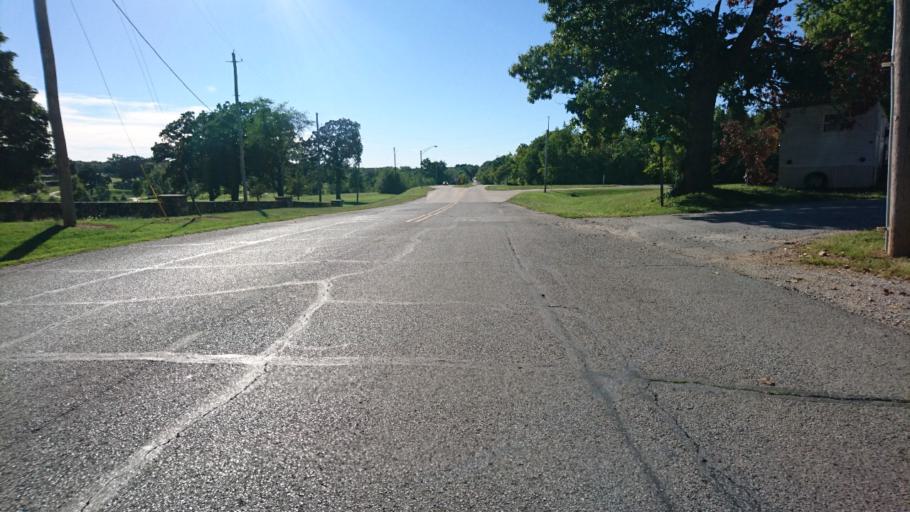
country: US
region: Missouri
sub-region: Jasper County
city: Carthage
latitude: 37.1766
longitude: -94.3378
